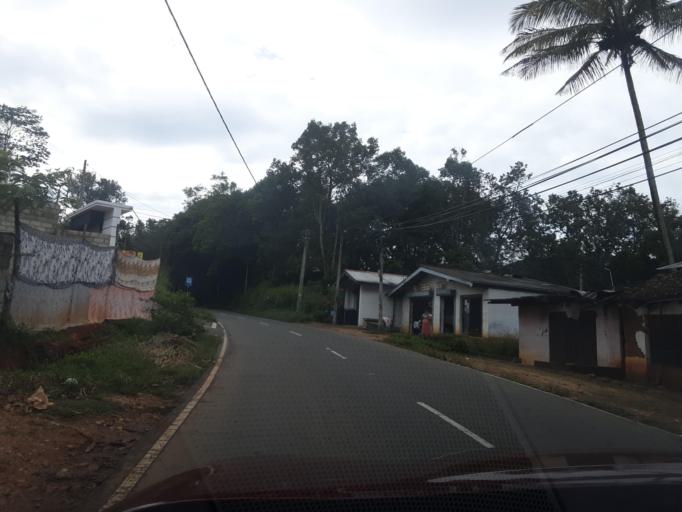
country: LK
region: Uva
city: Haputale
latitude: 6.8566
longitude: 80.9676
